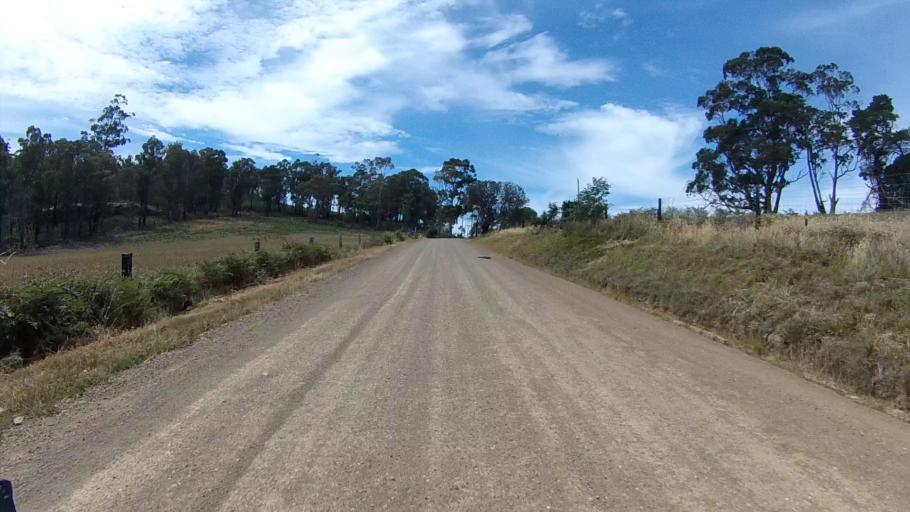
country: AU
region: Tasmania
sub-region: Sorell
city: Sorell
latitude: -42.7886
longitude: 147.7058
